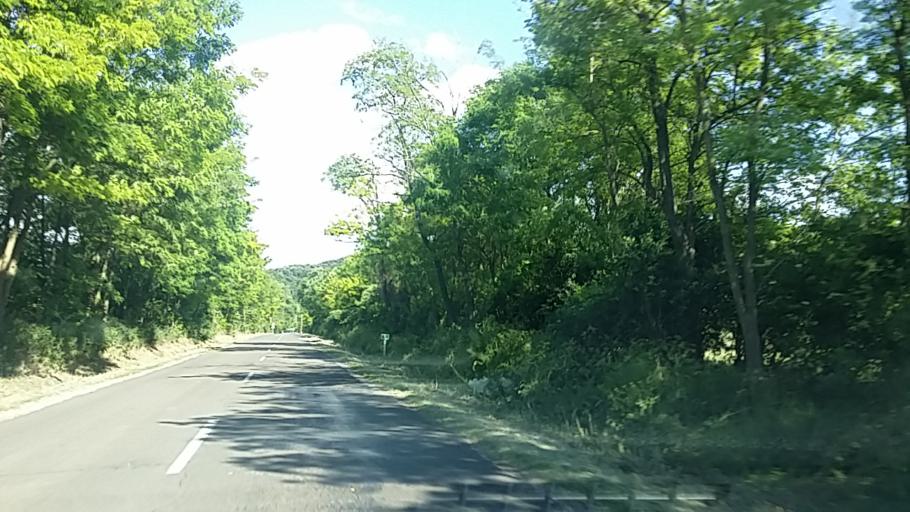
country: HU
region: Komarom-Esztergom
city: Bajna
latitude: 47.5984
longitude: 18.6088
